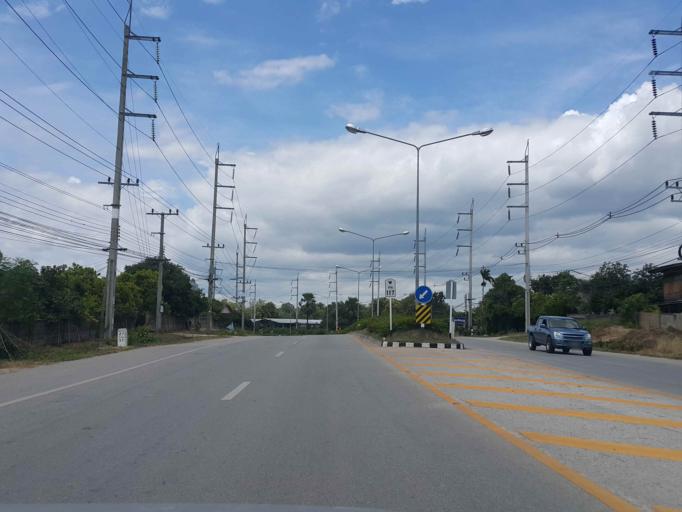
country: TH
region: Lamphun
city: Ban Hong
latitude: 18.3405
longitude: 98.8153
